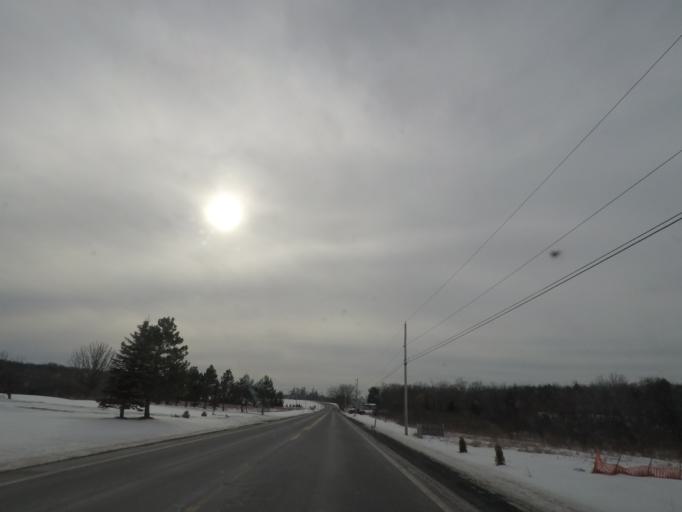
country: US
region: New York
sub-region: Albany County
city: Altamont
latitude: 42.6906
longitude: -74.0645
